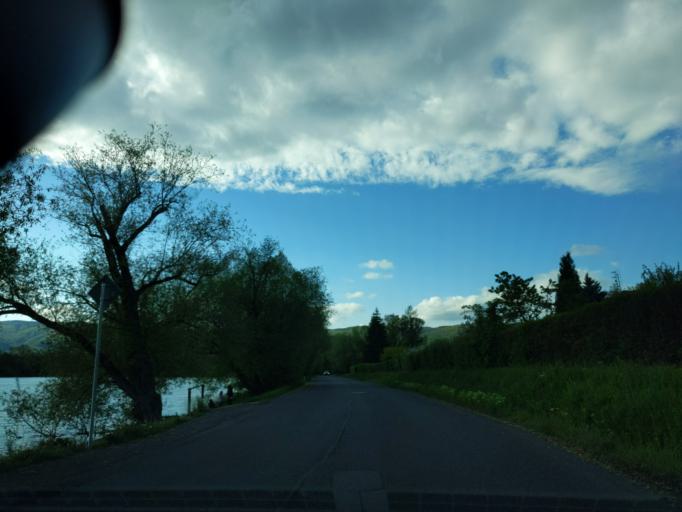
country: CZ
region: Ustecky
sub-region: Okres Usti nad Labem
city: Usti nad Labem
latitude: 50.6955
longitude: 14.0030
